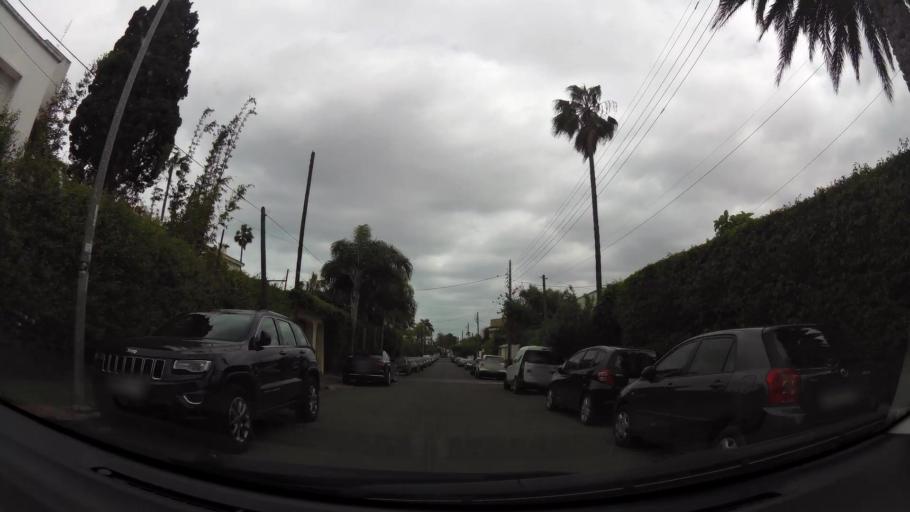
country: MA
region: Grand Casablanca
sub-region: Casablanca
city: Casablanca
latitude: 33.5711
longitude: -7.6585
